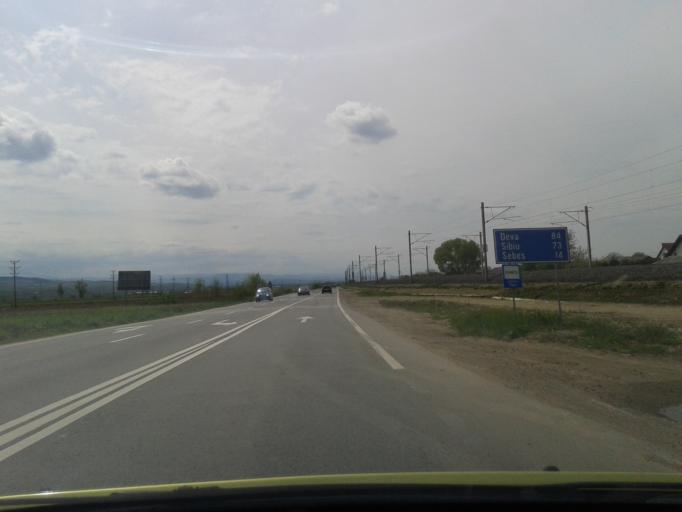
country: RO
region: Alba
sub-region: Municipiul Alba Iulia
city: Alba Iulia
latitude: 46.0712
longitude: 23.5959
